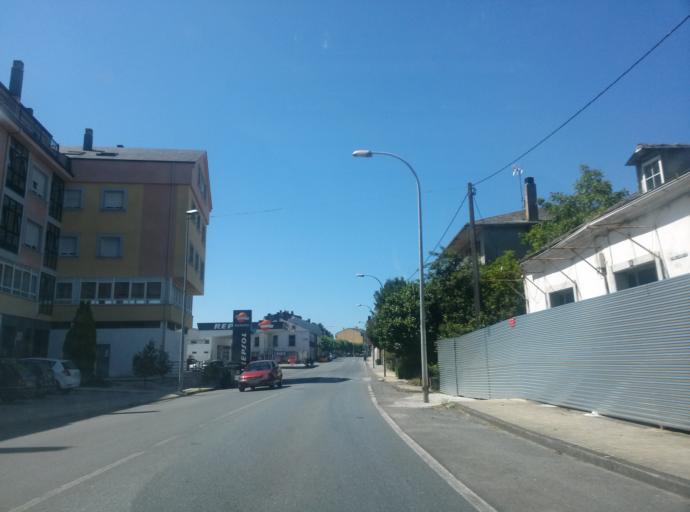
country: ES
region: Galicia
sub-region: Provincia de Lugo
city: Mos
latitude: 43.1370
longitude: -7.4914
